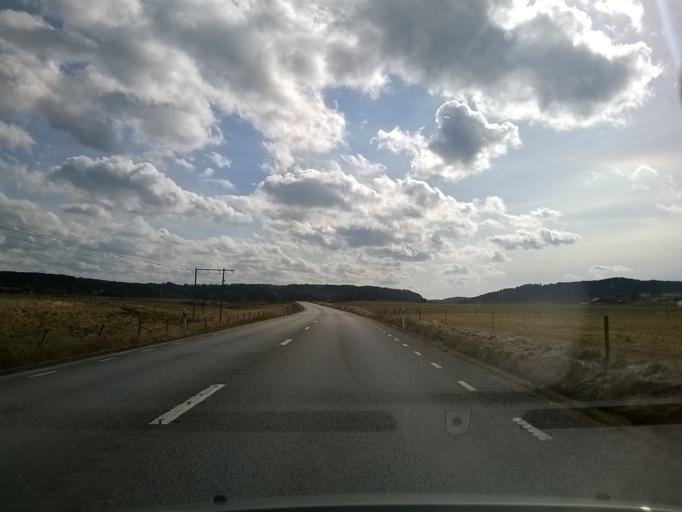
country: SE
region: Vaestra Goetaland
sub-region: Orust
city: Henan
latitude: 58.1710
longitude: 11.7000
